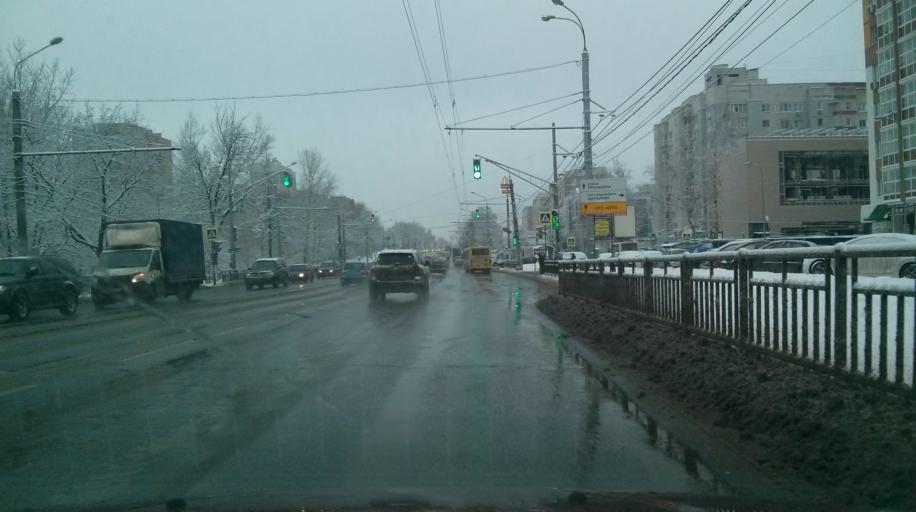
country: RU
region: Nizjnij Novgorod
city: Nizhniy Novgorod
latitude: 56.2367
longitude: 43.9551
